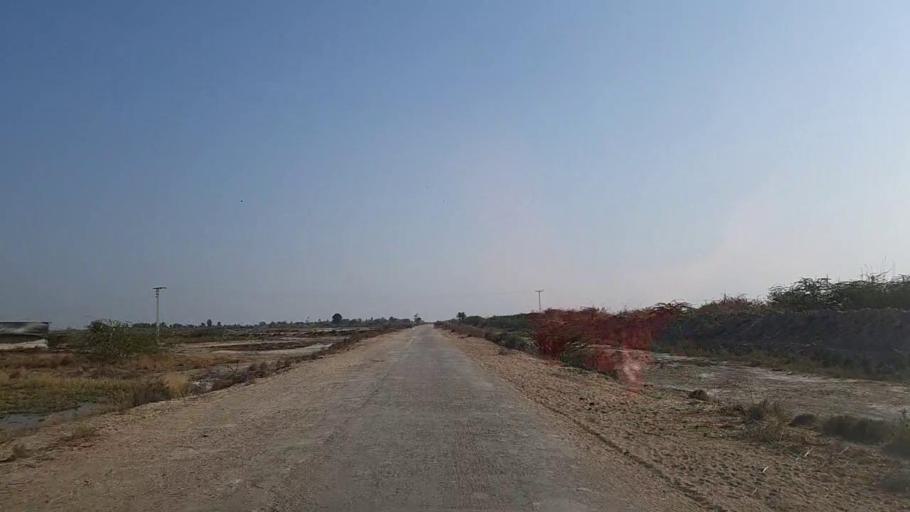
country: PK
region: Sindh
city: Tando Mittha Khan
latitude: 25.9260
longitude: 69.0662
